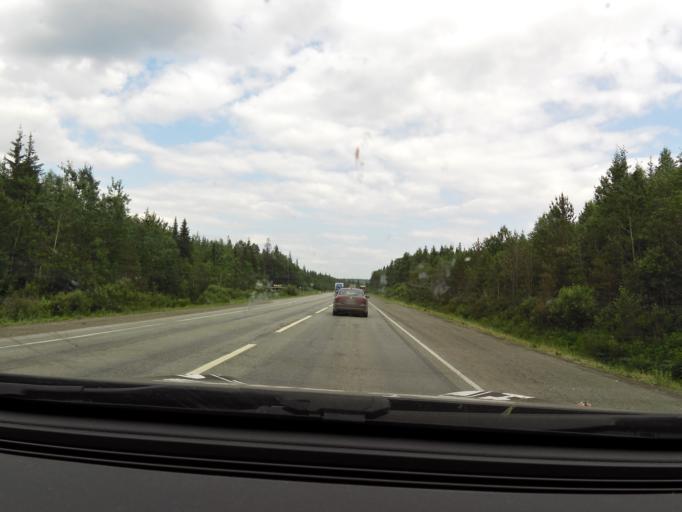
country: RU
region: Sverdlovsk
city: Bilimbay
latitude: 56.8525
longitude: 59.7873
